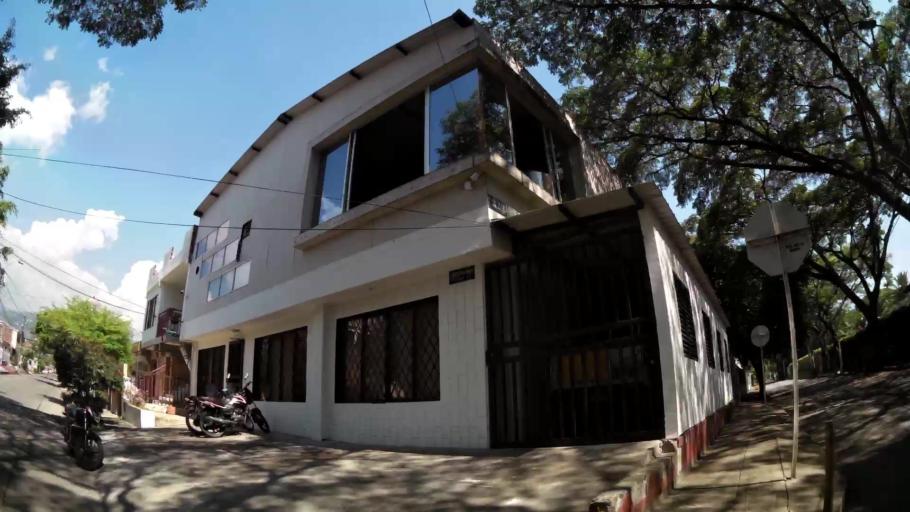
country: CO
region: Valle del Cauca
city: Cali
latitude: 3.4222
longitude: -76.5326
